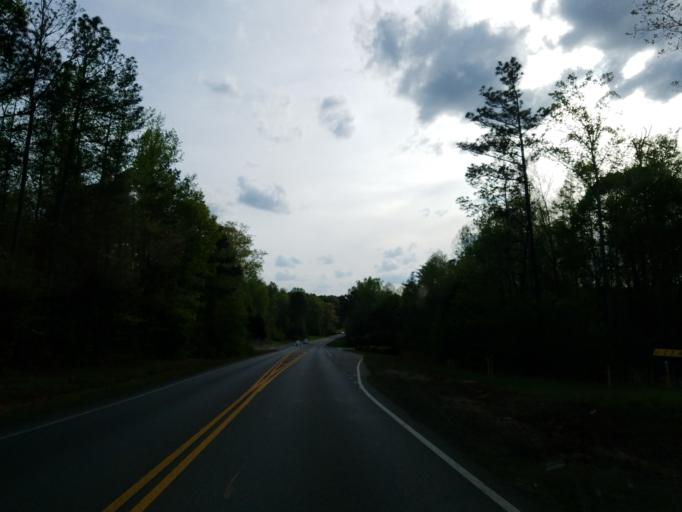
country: US
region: Georgia
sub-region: Cherokee County
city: Ball Ground
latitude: 34.2619
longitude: -84.3171
